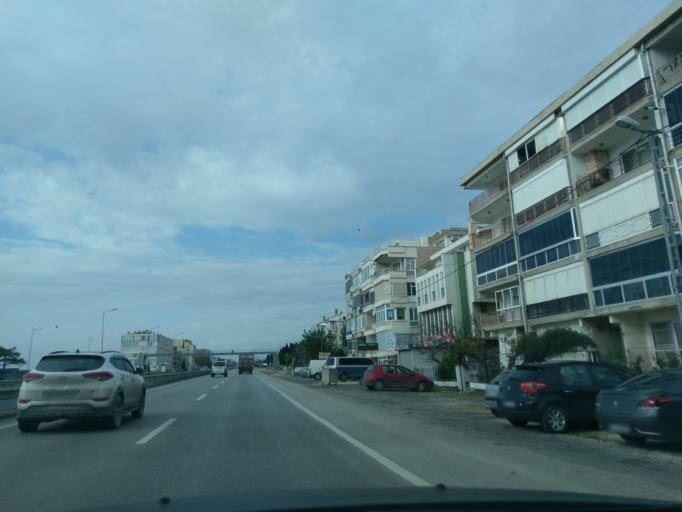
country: TR
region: Istanbul
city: Celaliye
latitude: 41.0452
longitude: 28.4094
